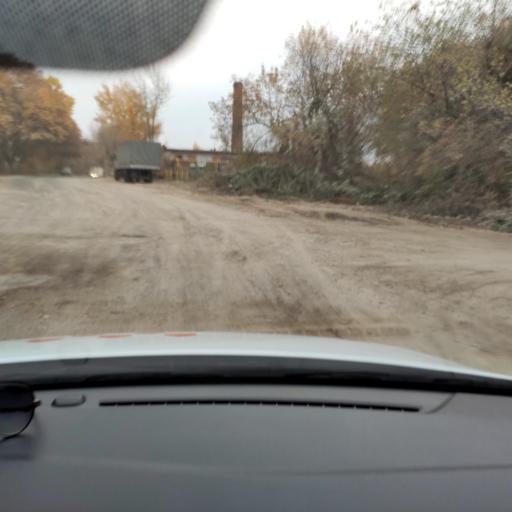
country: RU
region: Tatarstan
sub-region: Gorod Kazan'
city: Kazan
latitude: 55.7441
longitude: 49.0996
